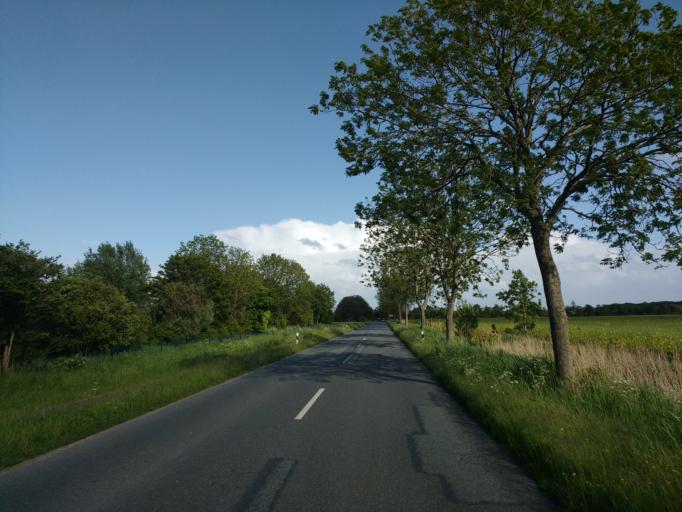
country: DE
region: Lower Saxony
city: Schillig
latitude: 53.6960
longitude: 8.0060
